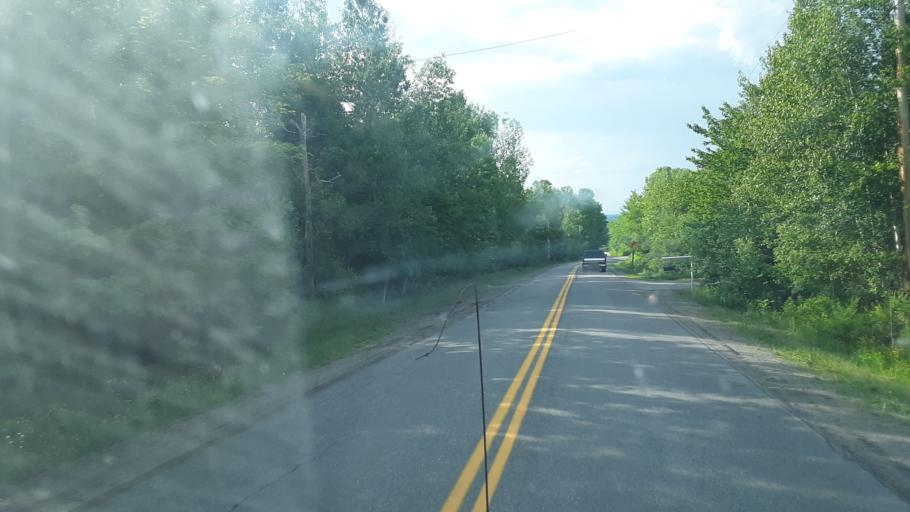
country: US
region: Maine
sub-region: Washington County
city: Calais
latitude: 45.0997
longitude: -67.5103
